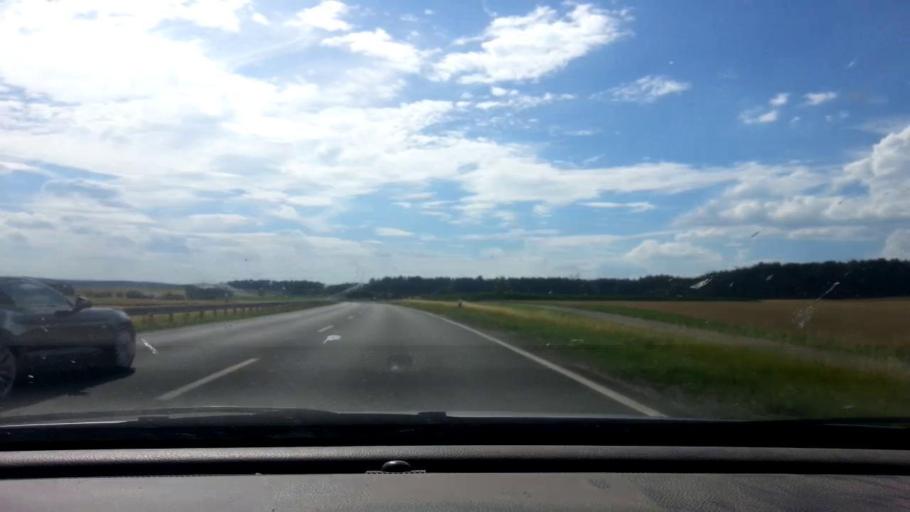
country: DE
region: Bavaria
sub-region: Upper Franconia
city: Speichersdorf
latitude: 49.8799
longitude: 11.7600
